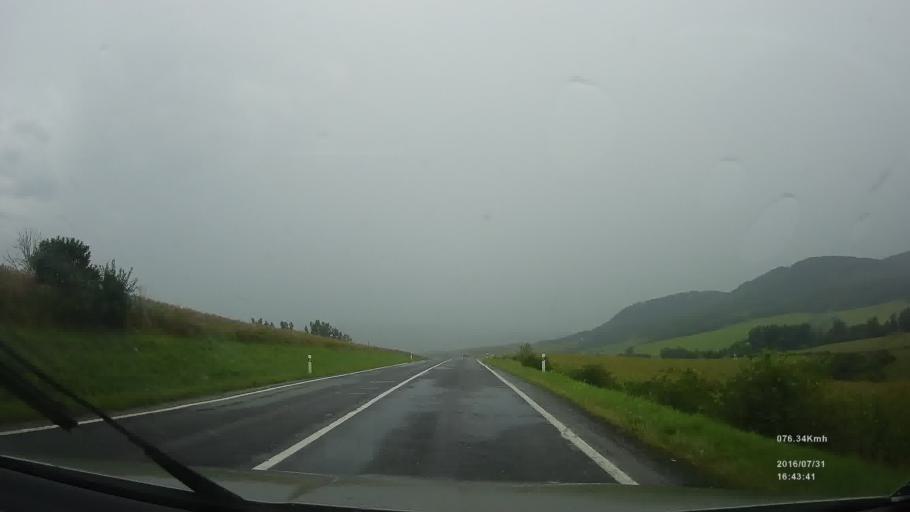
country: SK
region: Presovsky
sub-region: Okres Presov
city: Presov
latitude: 49.0833
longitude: 21.3162
